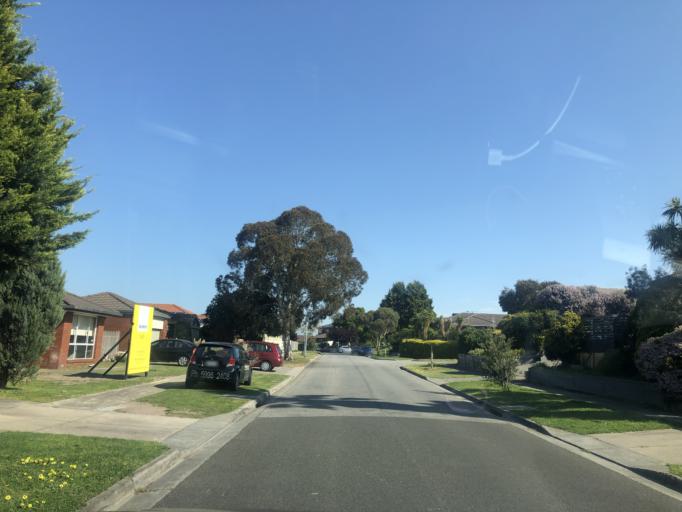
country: AU
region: Victoria
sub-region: Casey
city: Narre Warren South
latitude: -38.0452
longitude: 145.2731
